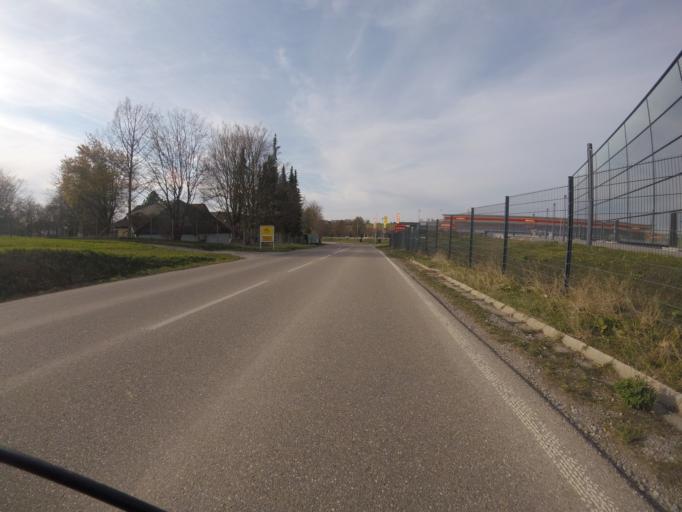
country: DE
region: Baden-Wuerttemberg
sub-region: Regierungsbezirk Stuttgart
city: Kirchberg an der Murr
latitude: 48.9418
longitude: 9.3521
